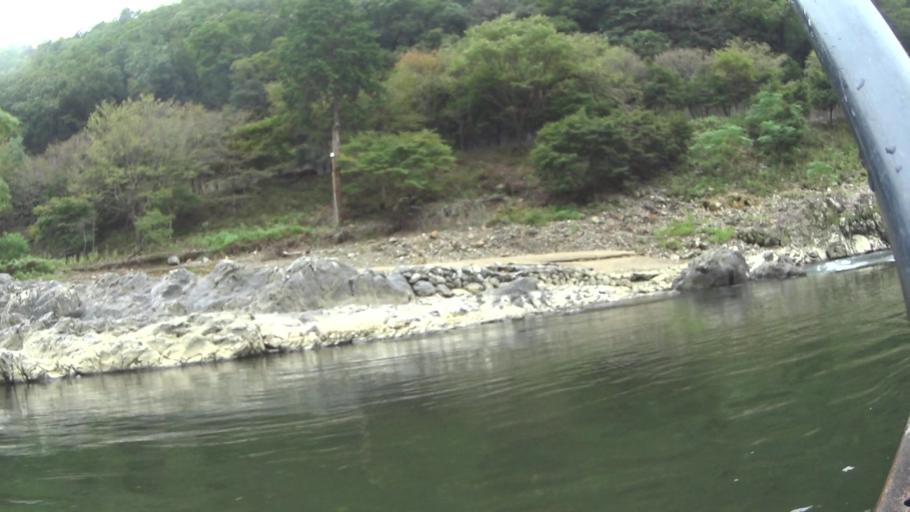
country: JP
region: Kyoto
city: Kameoka
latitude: 35.0251
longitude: 135.6548
